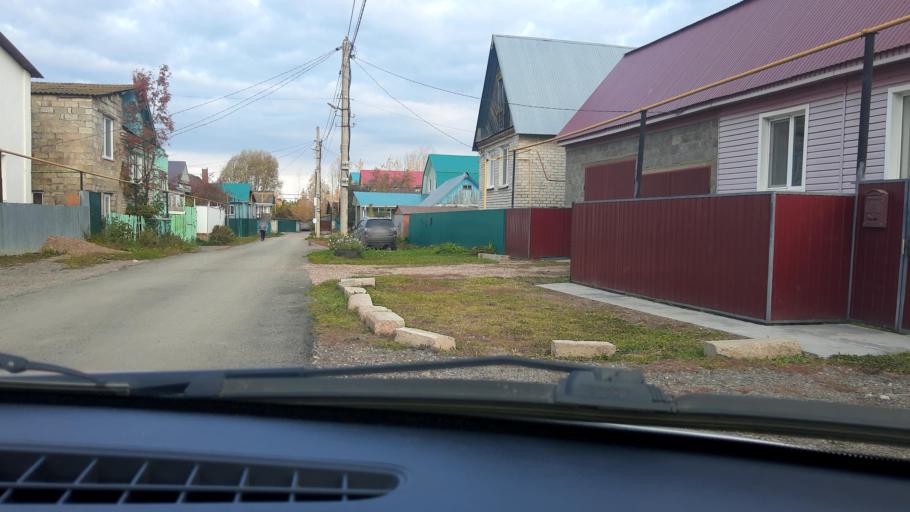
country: RU
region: Bashkortostan
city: Ufa
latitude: 54.7401
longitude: 55.9241
